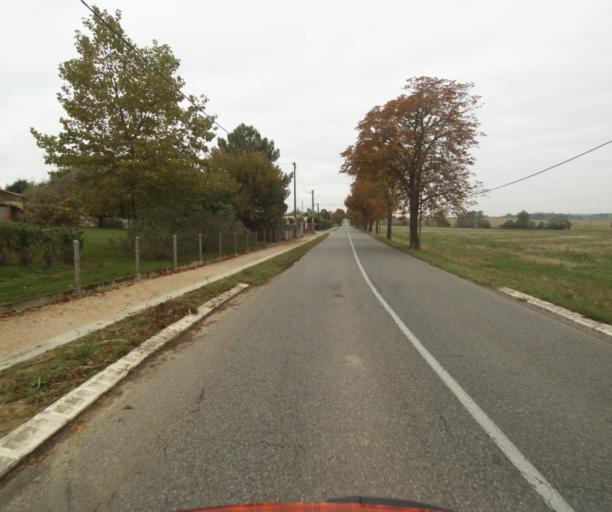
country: FR
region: Midi-Pyrenees
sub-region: Departement du Tarn-et-Garonne
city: Verdun-sur-Garonne
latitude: 43.8046
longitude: 1.2119
